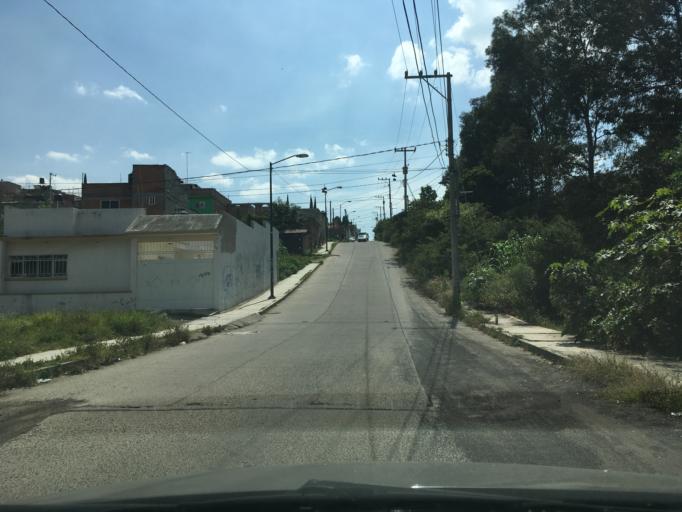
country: MX
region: Michoacan
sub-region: Morelia
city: Montana Monarca (Punta Altozano)
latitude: 19.6636
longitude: -101.1948
